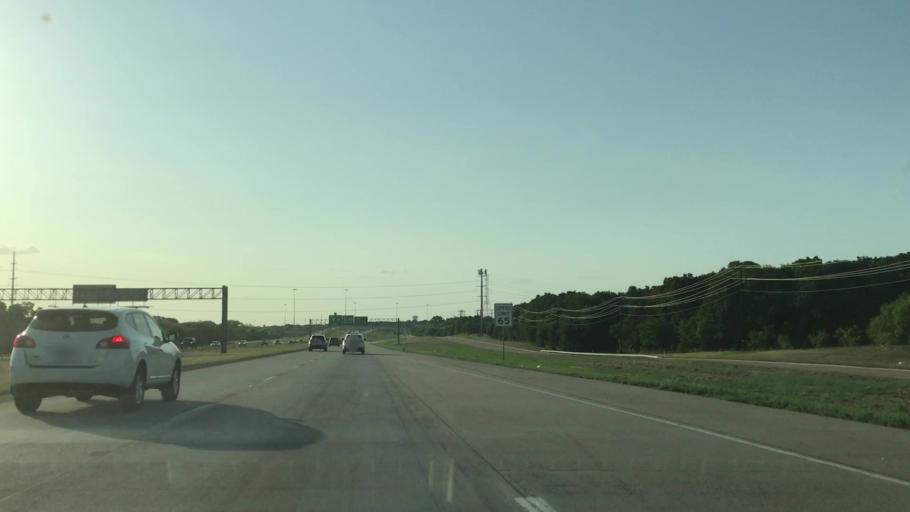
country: US
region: Texas
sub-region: Tarrant County
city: Grapevine
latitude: 32.8968
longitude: -97.0885
